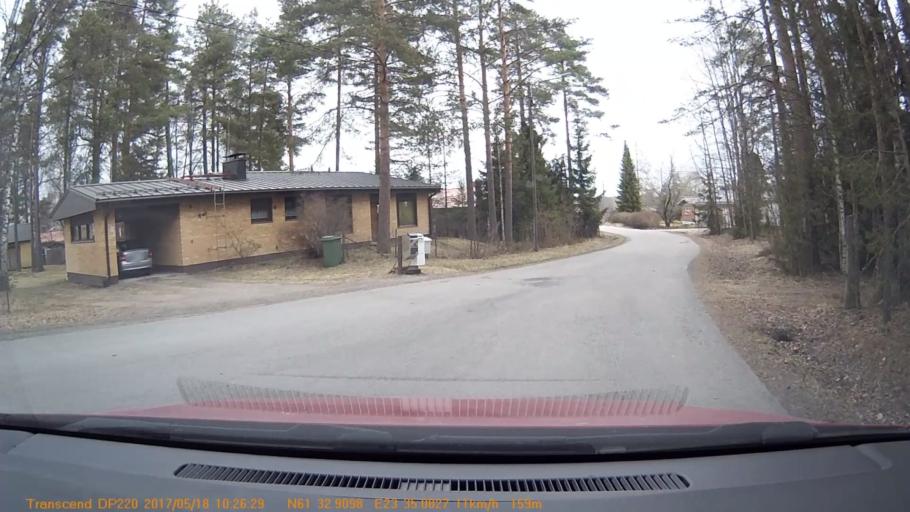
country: FI
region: Pirkanmaa
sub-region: Tampere
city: Yloejaervi
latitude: 61.5485
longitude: 23.5848
